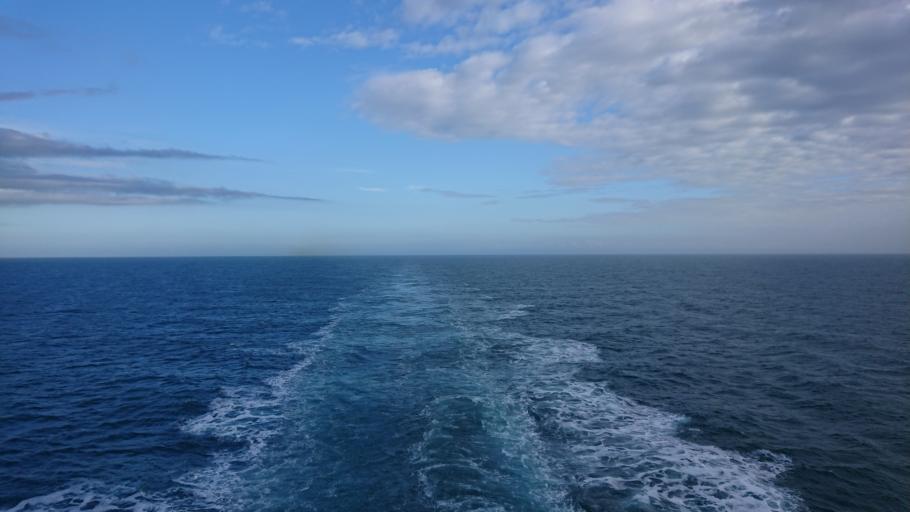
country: GB
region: Wales
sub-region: Pembrokeshire
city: Saint David's
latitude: 52.1364
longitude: -5.6262
